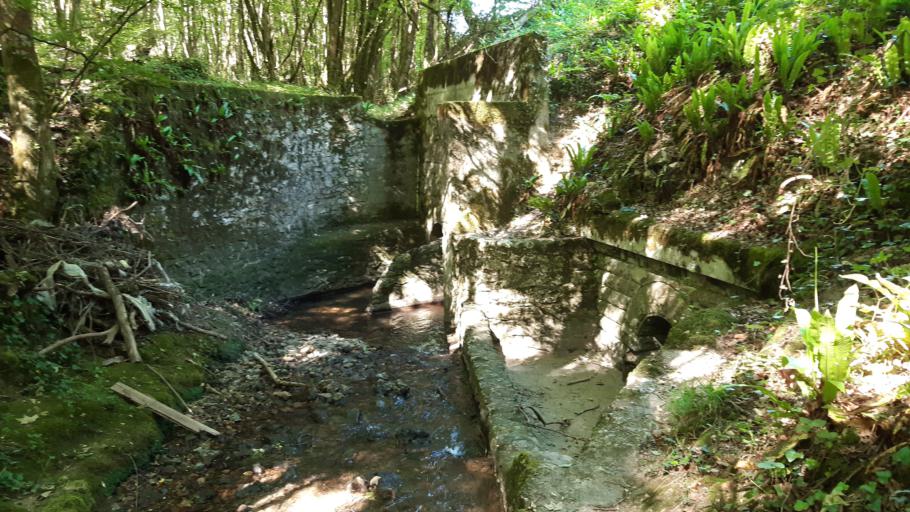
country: FR
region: Centre
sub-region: Departement d'Indre-et-Loire
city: Mettray
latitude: 47.4376
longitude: 0.6575
